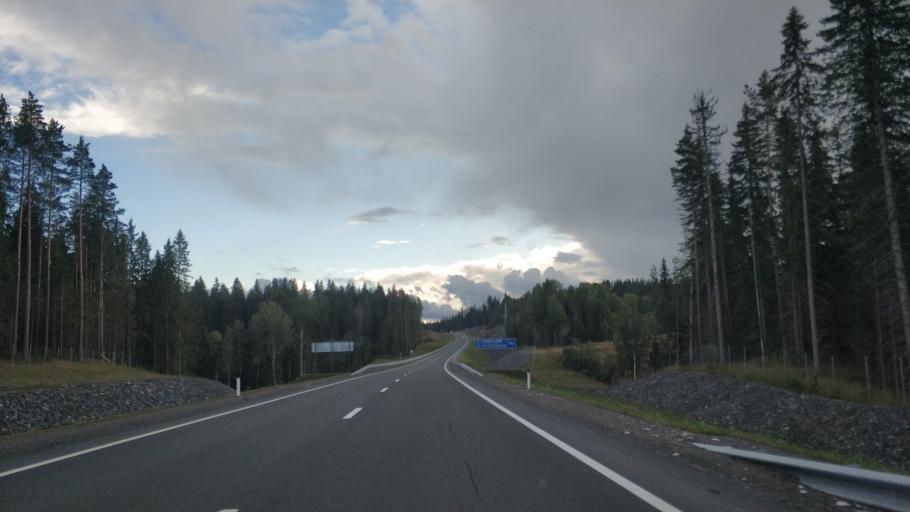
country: RU
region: Republic of Karelia
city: Lakhdenpokh'ya
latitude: 61.4726
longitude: 30.0057
